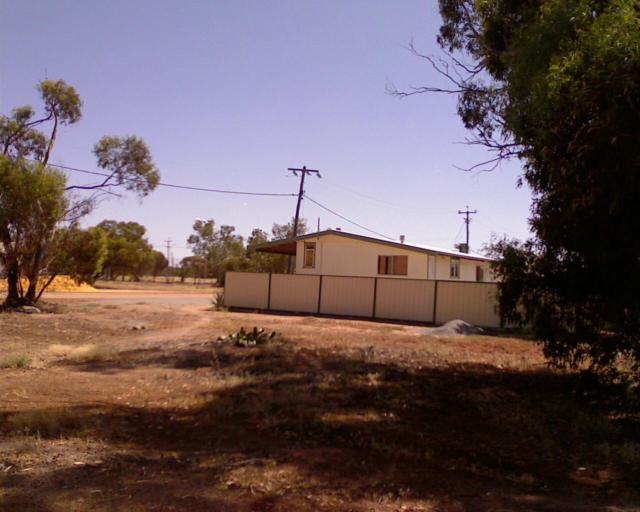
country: AU
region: Western Australia
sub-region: Moora
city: Moora
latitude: -29.9869
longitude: 116.5692
